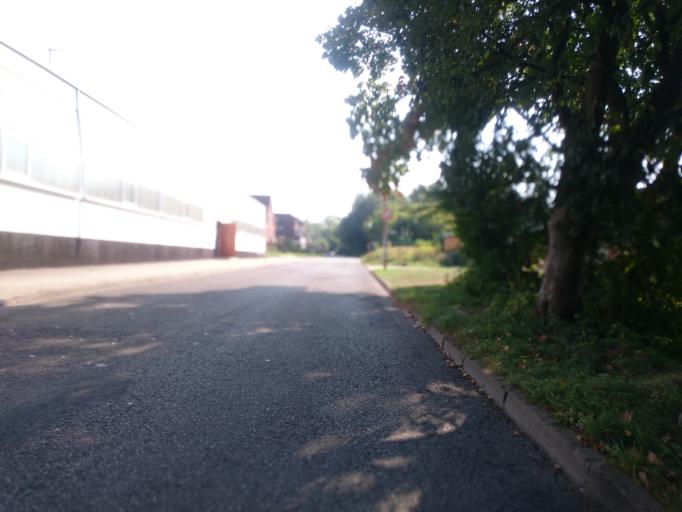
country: DE
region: Mecklenburg-Vorpommern
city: Barth
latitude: 54.3516
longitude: 12.7190
